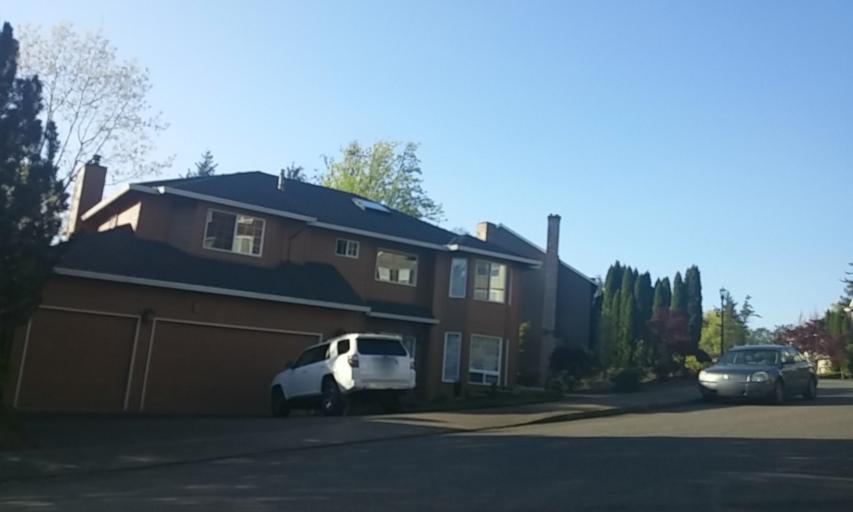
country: US
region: Oregon
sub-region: Washington County
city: West Haven
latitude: 45.5409
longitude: -122.7843
